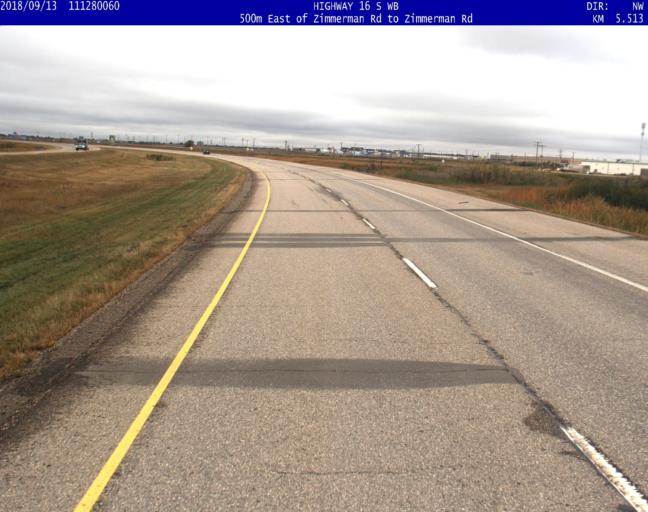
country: CA
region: Saskatchewan
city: Saskatoon
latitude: 52.0849
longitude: -106.5185
